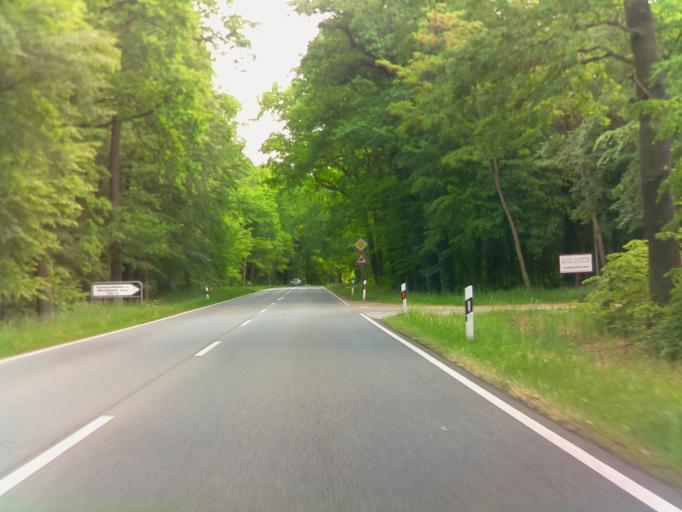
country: DE
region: Brandenburg
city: Nennhausen
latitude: 52.6245
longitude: 12.4505
